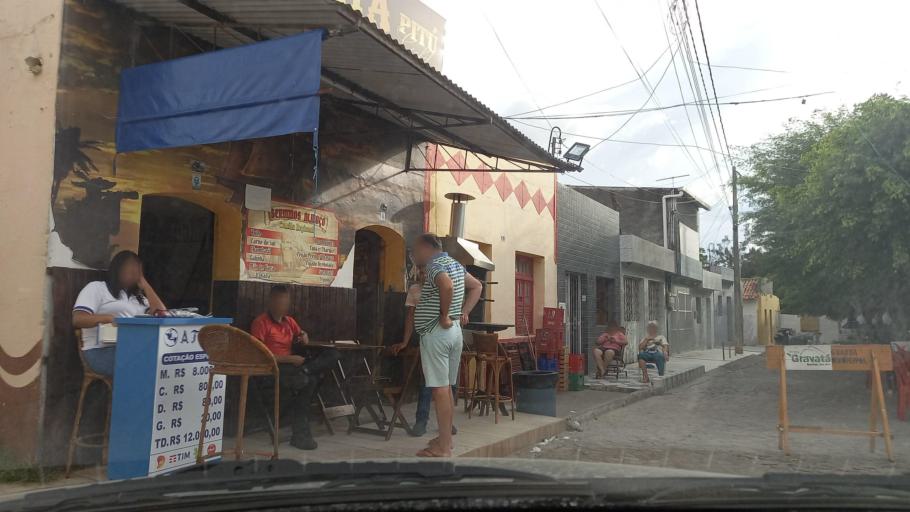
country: BR
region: Pernambuco
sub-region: Gravata
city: Gravata
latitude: -8.2035
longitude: -35.5650
